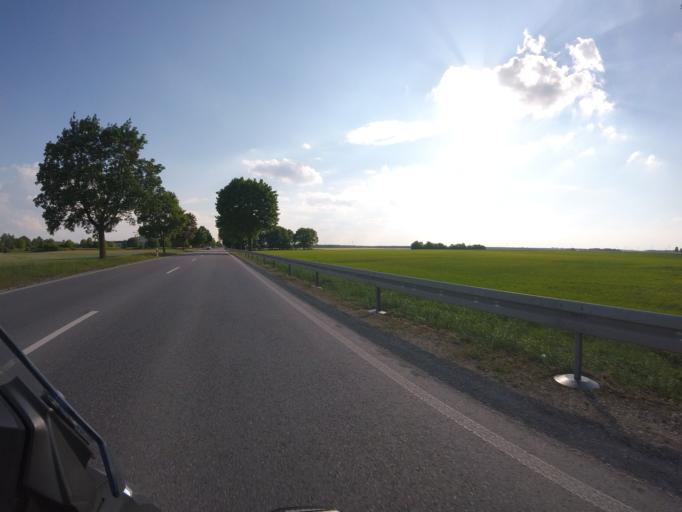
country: DE
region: Bavaria
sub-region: Upper Bavaria
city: Garching bei Munchen
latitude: 48.2732
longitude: 11.6680
